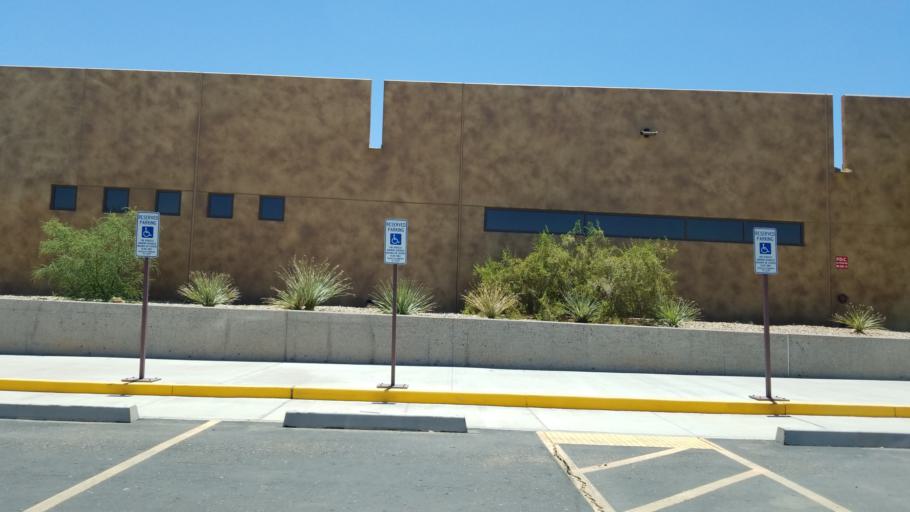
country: US
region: Arizona
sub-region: Maricopa County
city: Litchfield Park
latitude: 33.5152
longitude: -112.2964
